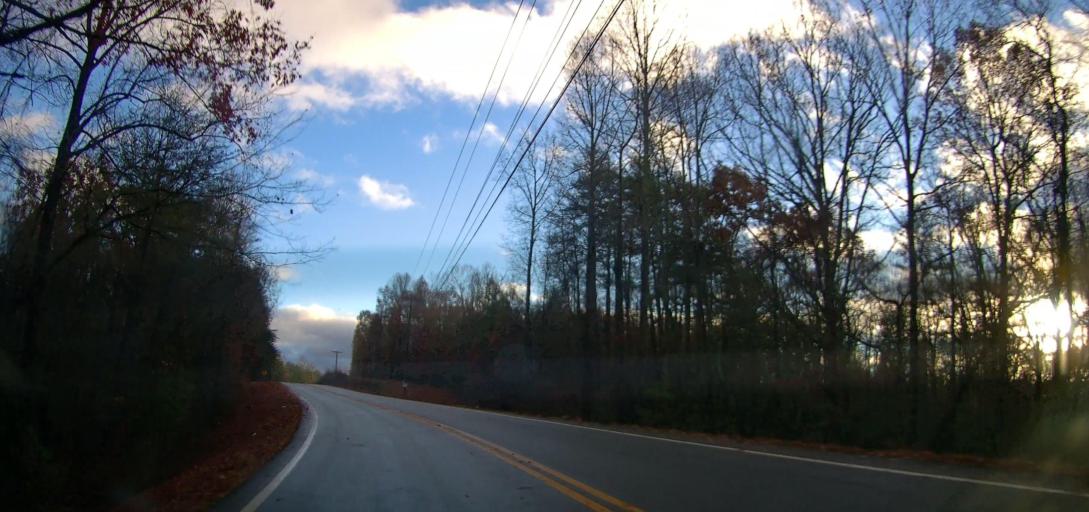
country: US
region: Georgia
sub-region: White County
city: Cleveland
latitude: 34.6277
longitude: -83.8056
